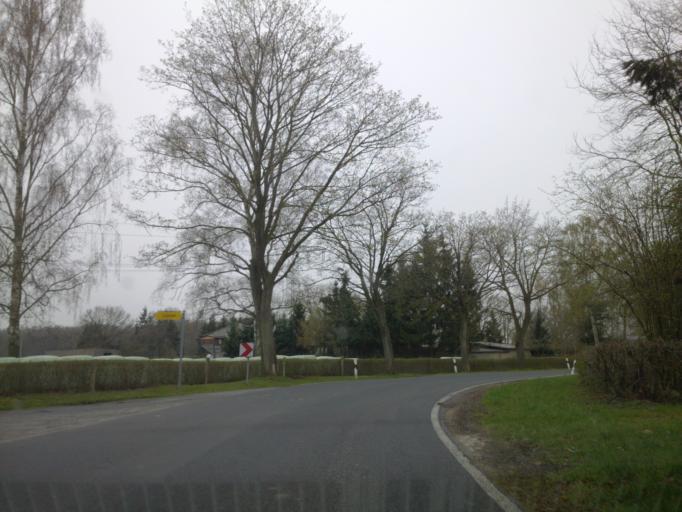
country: DE
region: Mecklenburg-Vorpommern
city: Tribsees
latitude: 54.1773
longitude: 12.7402
